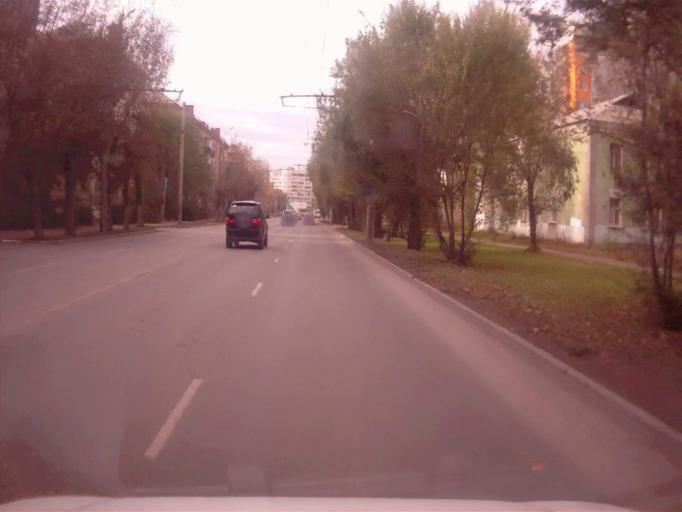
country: RU
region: Chelyabinsk
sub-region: Gorod Chelyabinsk
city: Chelyabinsk
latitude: 55.1154
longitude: 61.4491
